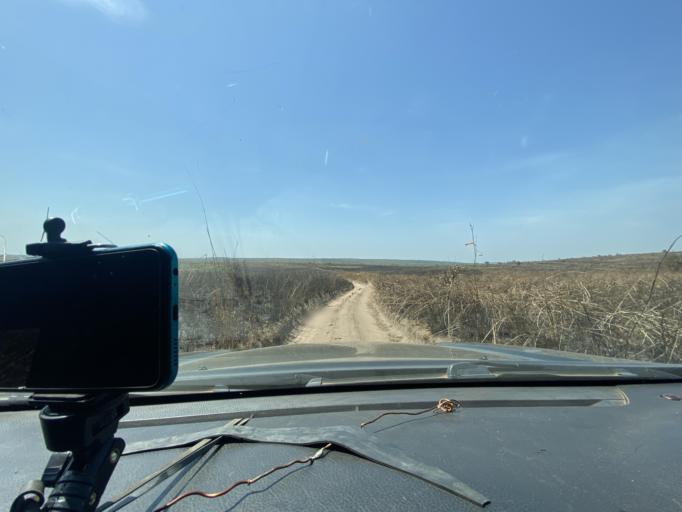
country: CD
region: Kasai-Oriental
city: Kabinda
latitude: -5.9399
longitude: 24.8097
